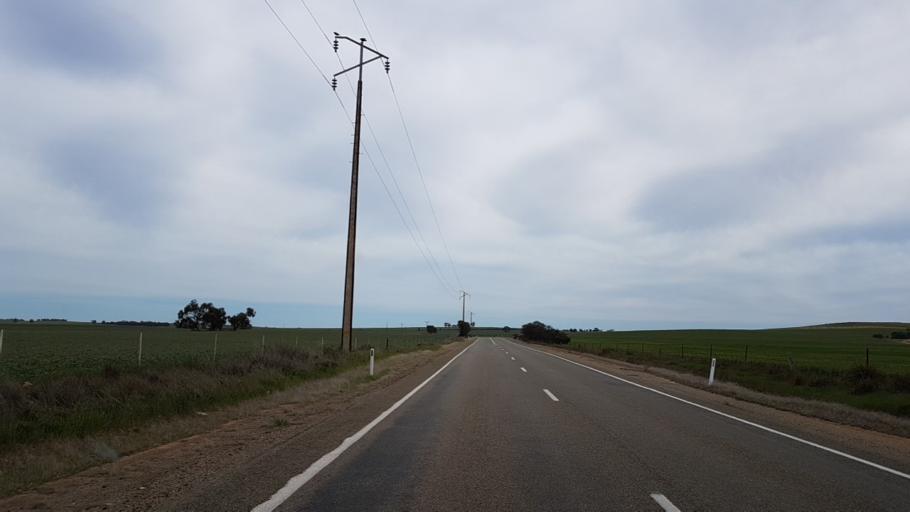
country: AU
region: South Australia
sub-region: Port Pirie City and Dists
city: Crystal Brook
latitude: -33.2698
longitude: 138.3195
